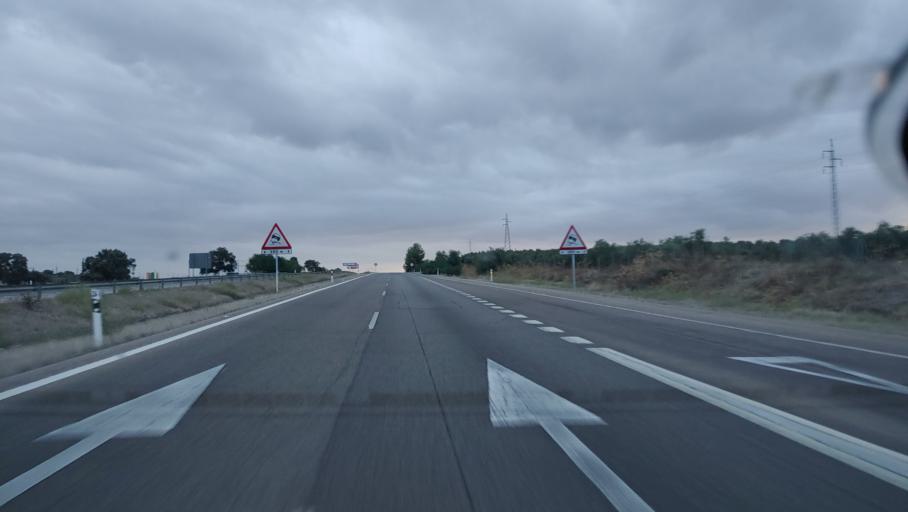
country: ES
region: Andalusia
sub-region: Provincia de Jaen
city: Guarroman
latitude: 38.1573
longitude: -3.7160
